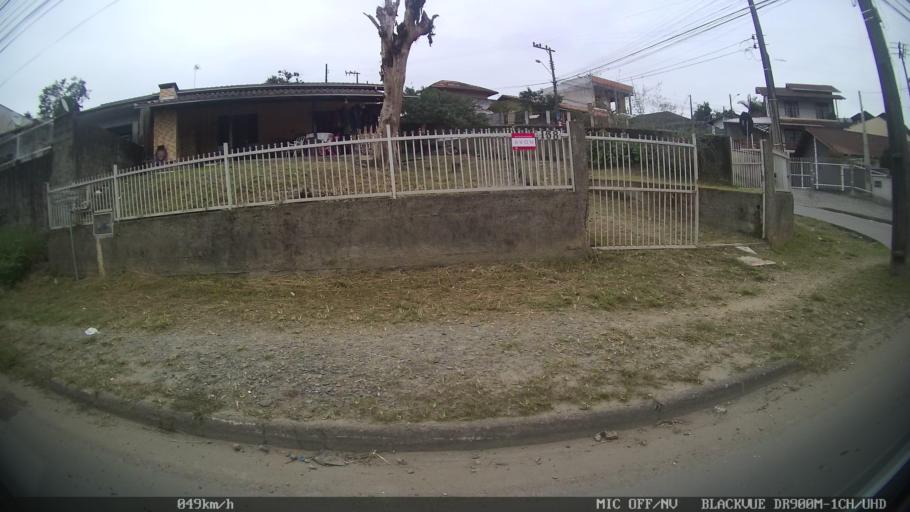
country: BR
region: Santa Catarina
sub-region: Joinville
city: Joinville
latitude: -26.3370
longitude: -48.8059
